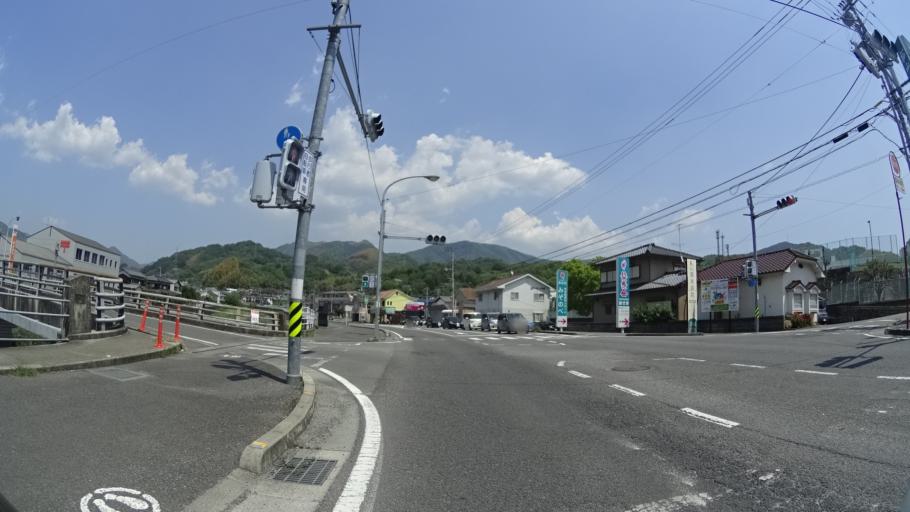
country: JP
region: Ehime
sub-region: Shikoku-chuo Shi
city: Matsuyama
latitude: 33.8504
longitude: 132.8060
